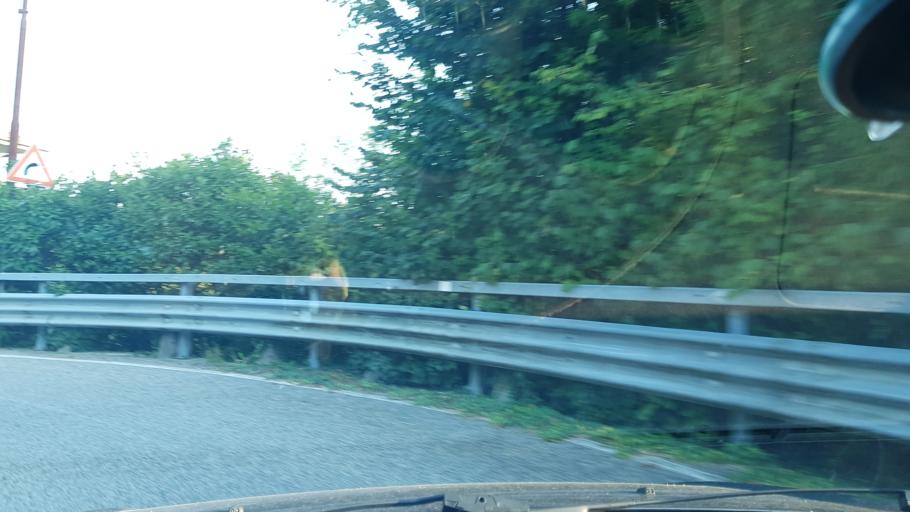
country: IT
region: Friuli Venezia Giulia
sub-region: Provincia di Gorizia
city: Gorizia
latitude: 45.9662
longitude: 13.6148
